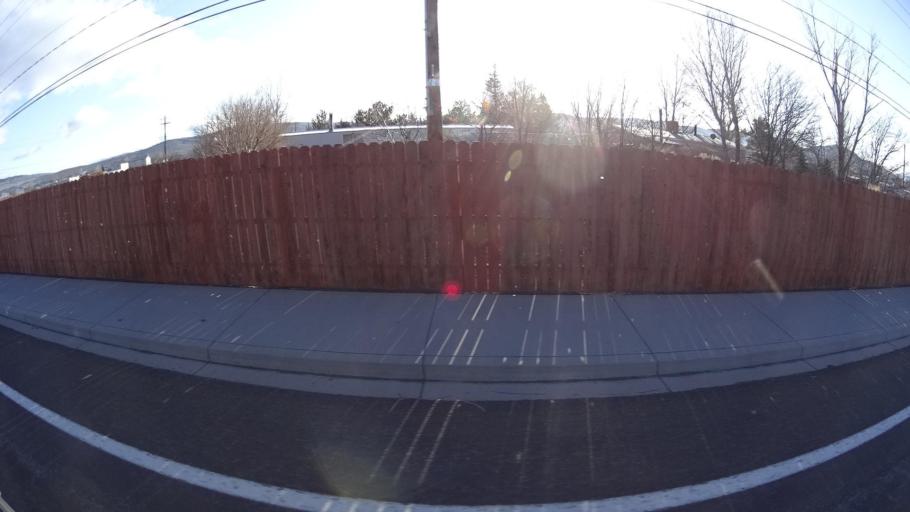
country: US
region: Nevada
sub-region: Washoe County
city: Cold Springs
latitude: 39.6859
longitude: -119.9785
